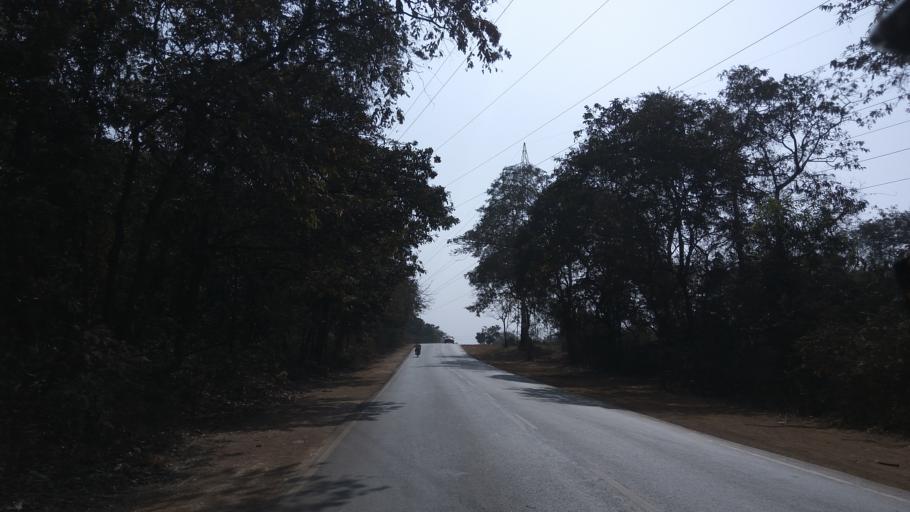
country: IN
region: Goa
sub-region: South Goa
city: Sanvordem
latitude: 15.3664
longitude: 74.1707
